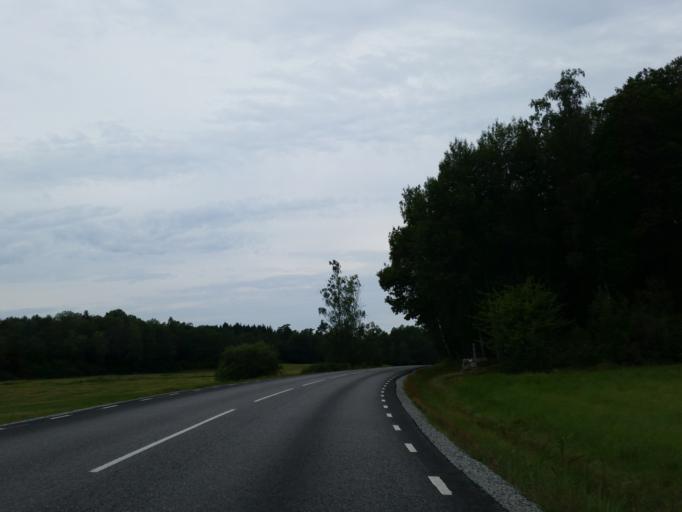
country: SE
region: Stockholm
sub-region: Salems Kommun
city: Ronninge
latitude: 59.2215
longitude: 17.7453
